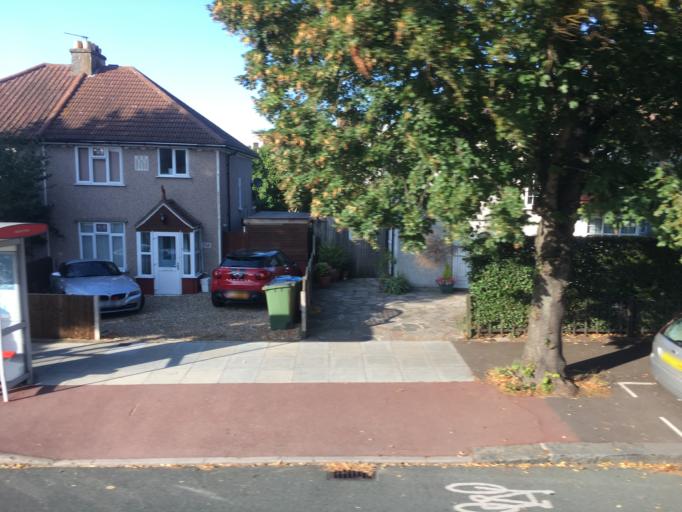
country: GB
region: England
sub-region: Greater London
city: Woolwich
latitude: 51.4604
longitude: 0.0453
